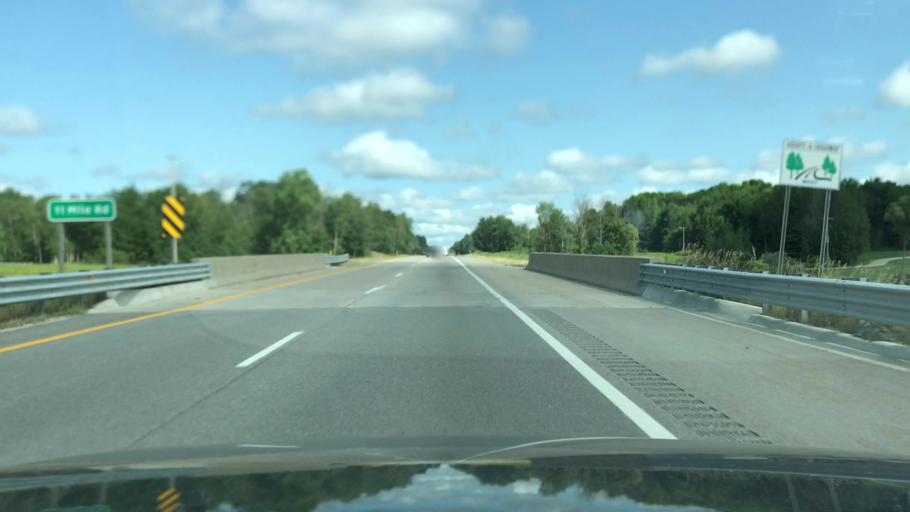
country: US
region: Michigan
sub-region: Mecosta County
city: Big Rapids
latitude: 43.6271
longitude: -85.5013
